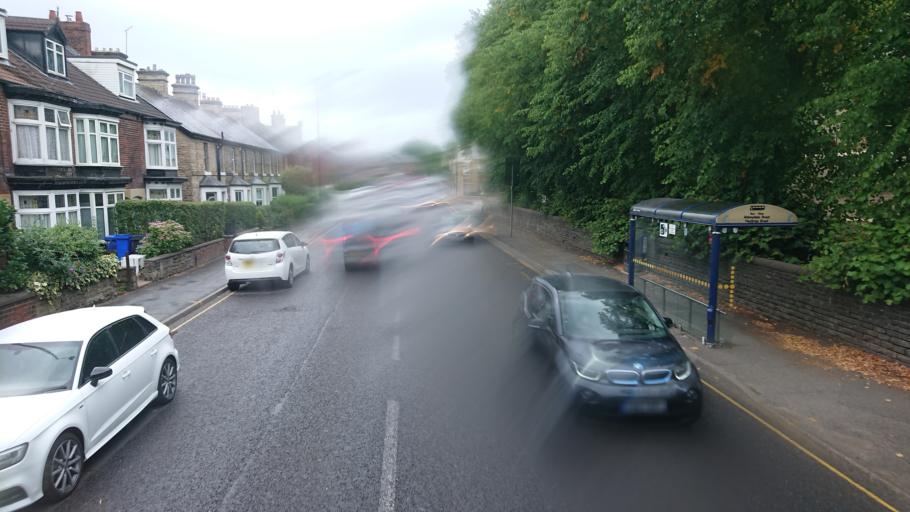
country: GB
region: England
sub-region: Sheffield
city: Sheffield
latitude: 53.3478
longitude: -1.4948
